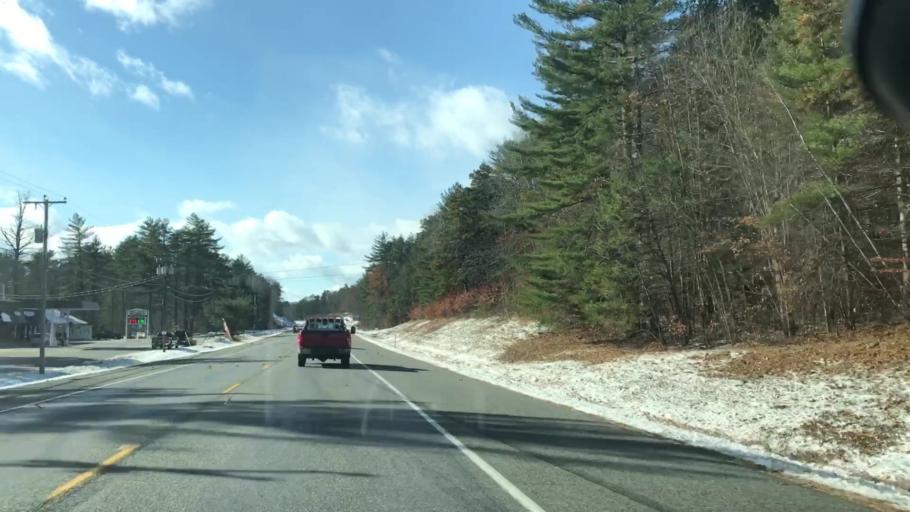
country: US
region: New Hampshire
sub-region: Carroll County
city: Freedom
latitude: 43.7851
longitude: -71.0954
